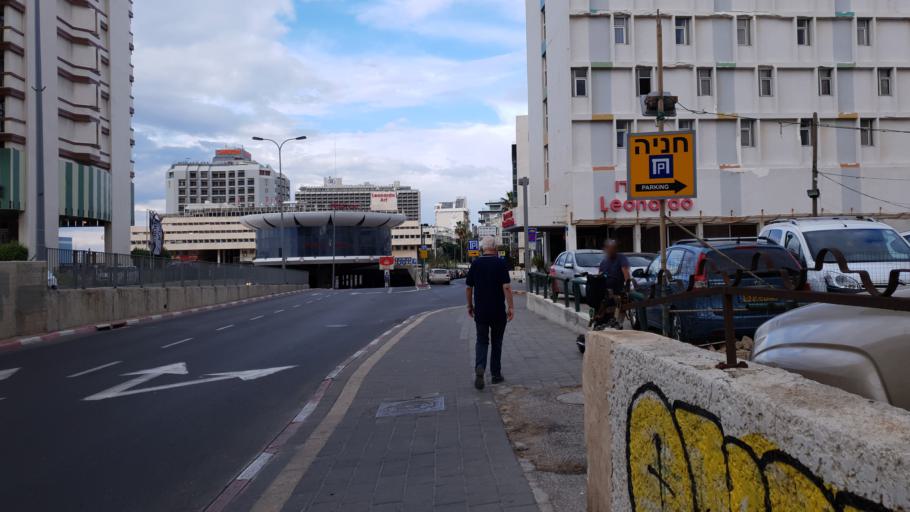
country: IL
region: Tel Aviv
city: Tel Aviv
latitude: 32.0840
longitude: 34.7694
